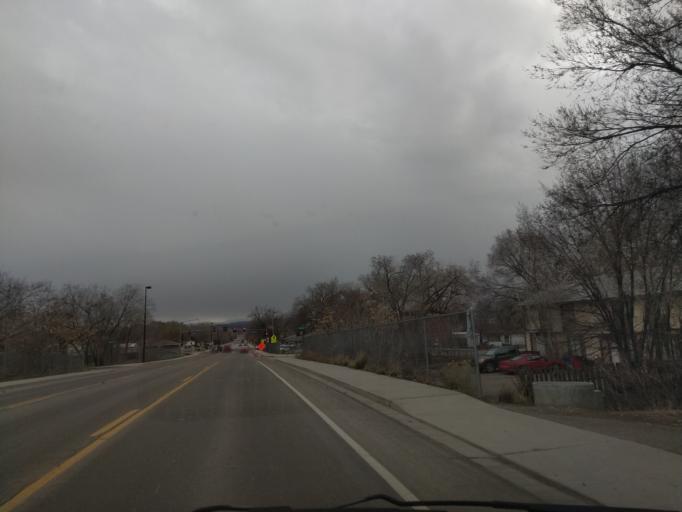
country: US
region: Colorado
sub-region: Mesa County
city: Fruitvale
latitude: 39.0861
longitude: -108.5152
